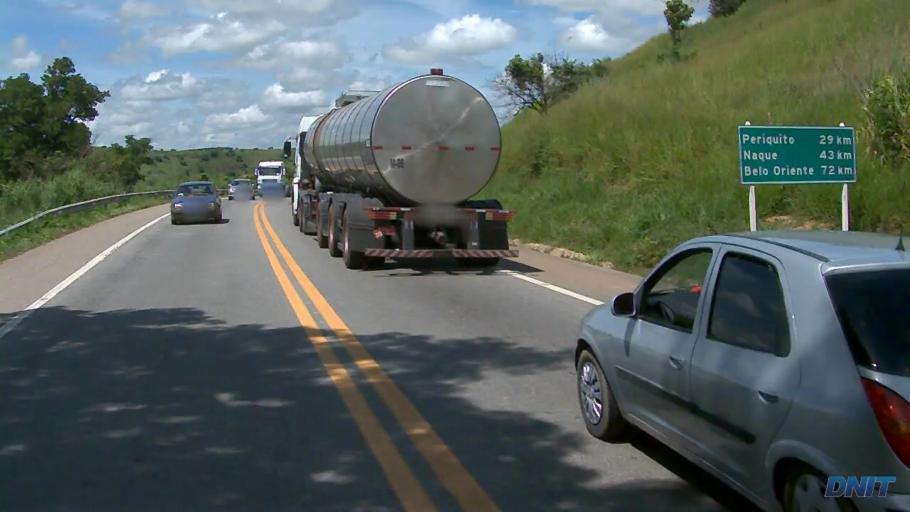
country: BR
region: Minas Gerais
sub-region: Governador Valadares
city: Governador Valadares
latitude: -18.9621
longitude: -42.0767
